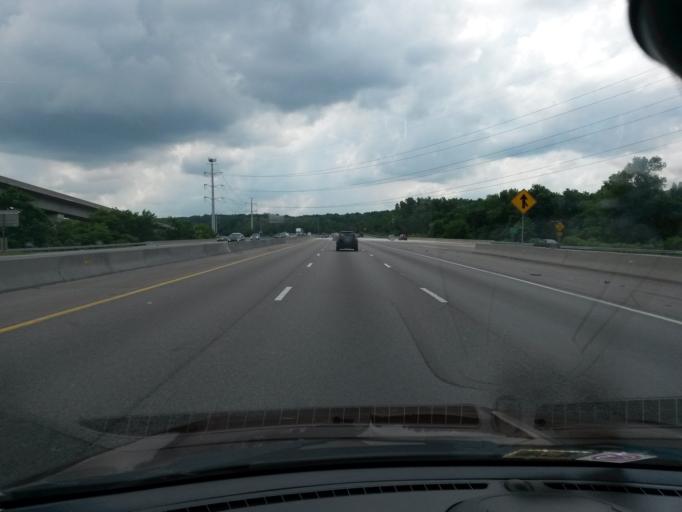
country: US
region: Virginia
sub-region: Chesterfield County
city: Bensley
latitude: 37.4390
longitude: -77.4289
